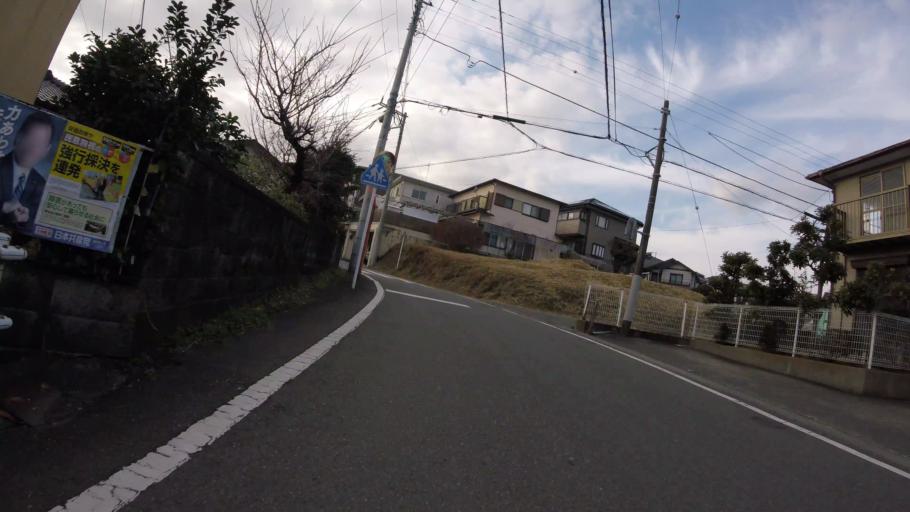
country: JP
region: Shizuoka
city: Mishima
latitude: 35.1463
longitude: 138.9126
